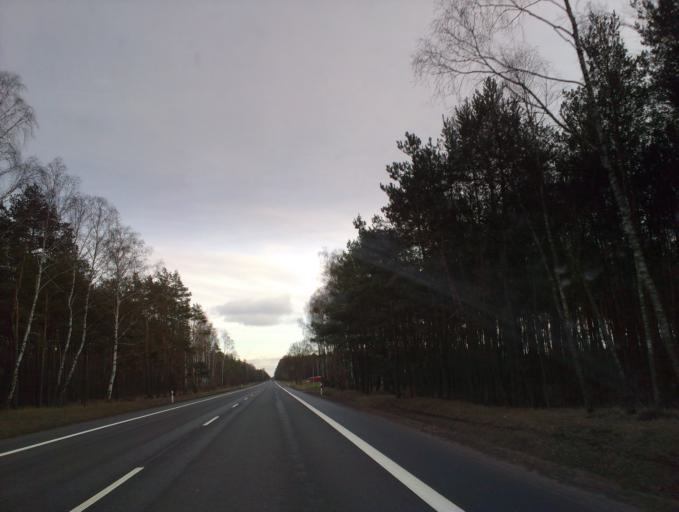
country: PL
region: Masovian Voivodeship
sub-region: Powiat sierpecki
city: Sierpc
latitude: 52.8772
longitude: 19.6049
